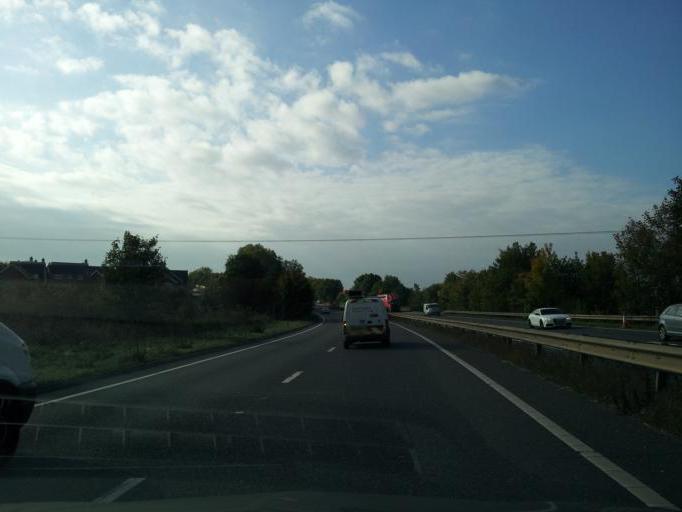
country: GB
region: England
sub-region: Northamptonshire
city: Towcester
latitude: 52.1354
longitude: -1.0027
